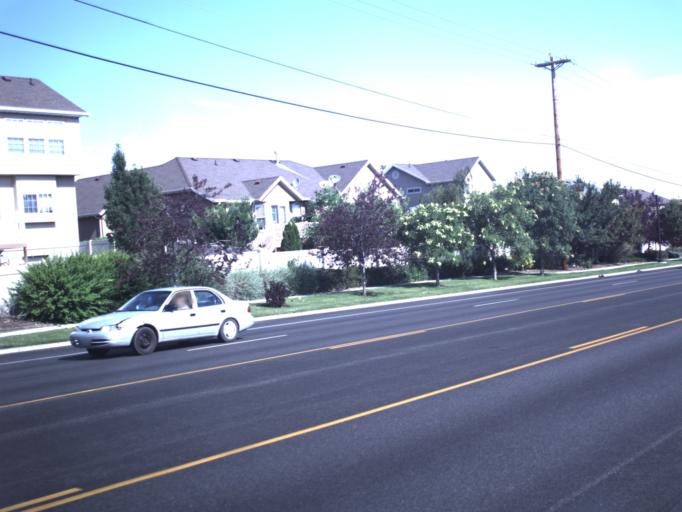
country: US
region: Utah
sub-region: Salt Lake County
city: Kearns
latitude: 40.6596
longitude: -112.0246
